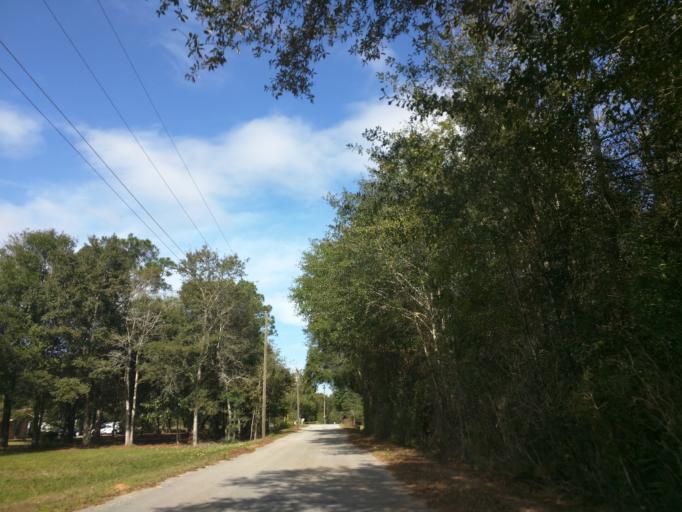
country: US
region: Florida
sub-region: Escambia County
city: Cantonment
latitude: 30.5530
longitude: -87.4056
